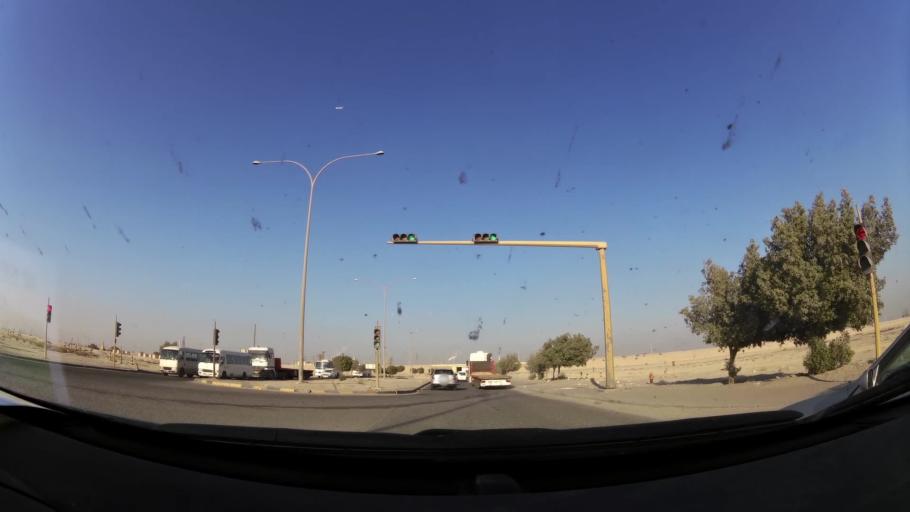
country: KW
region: Al Ahmadi
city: Al Fahahil
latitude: 29.0080
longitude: 48.1299
